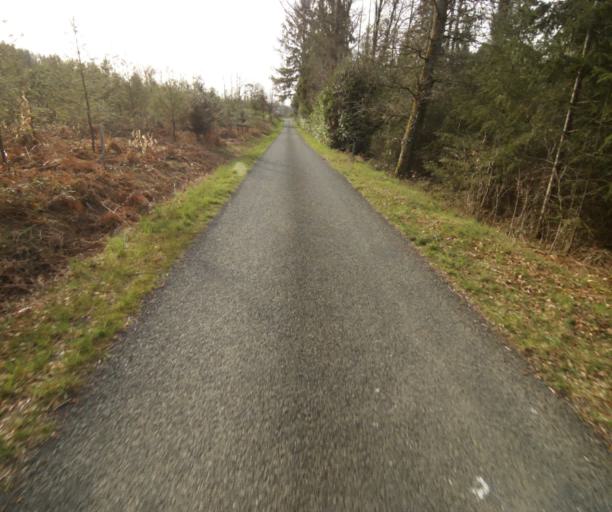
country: FR
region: Limousin
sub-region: Departement de la Correze
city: Chamboulive
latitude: 45.4360
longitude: 1.7610
